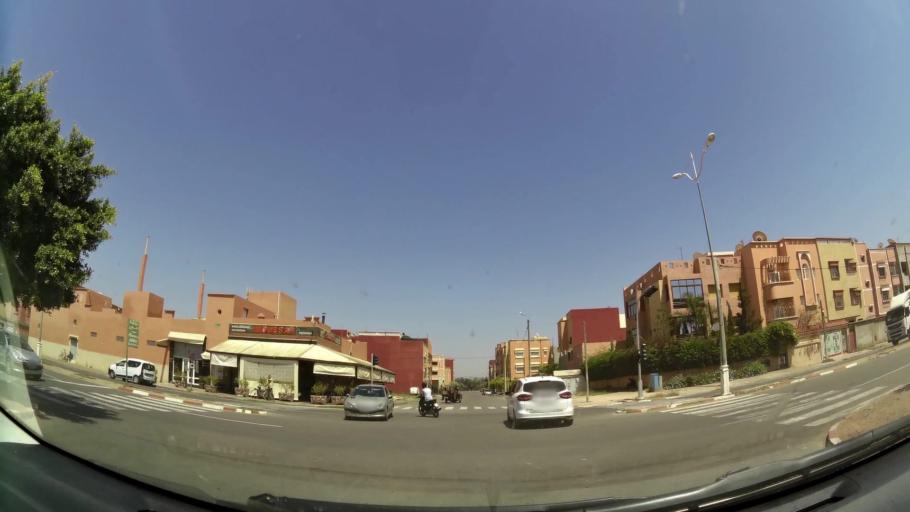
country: MA
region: Souss-Massa-Draa
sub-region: Inezgane-Ait Mellou
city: Inezgane
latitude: 30.3473
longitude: -9.4852
